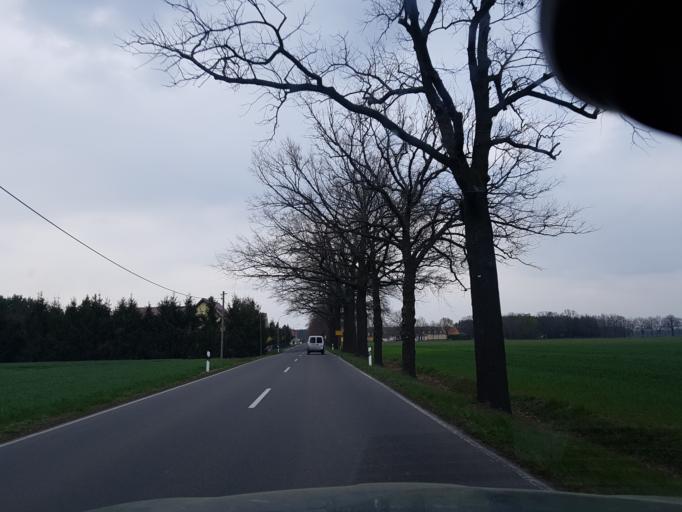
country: DE
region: Brandenburg
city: Schraden
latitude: 51.4261
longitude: 13.7057
